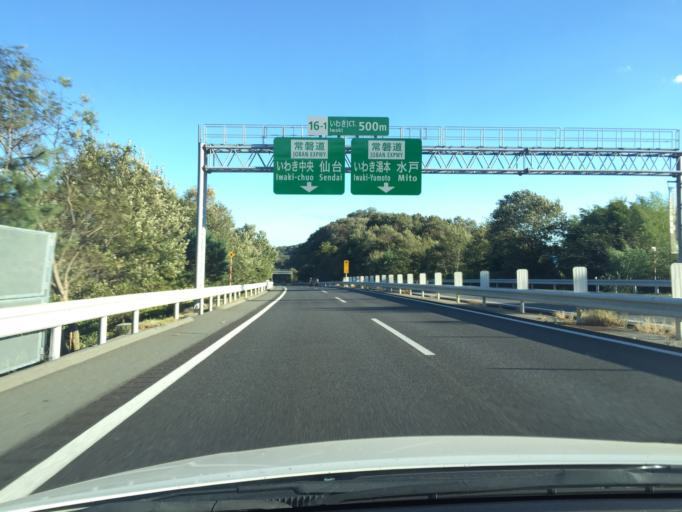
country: JP
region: Fukushima
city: Iwaki
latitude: 37.0422
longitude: 140.8107
